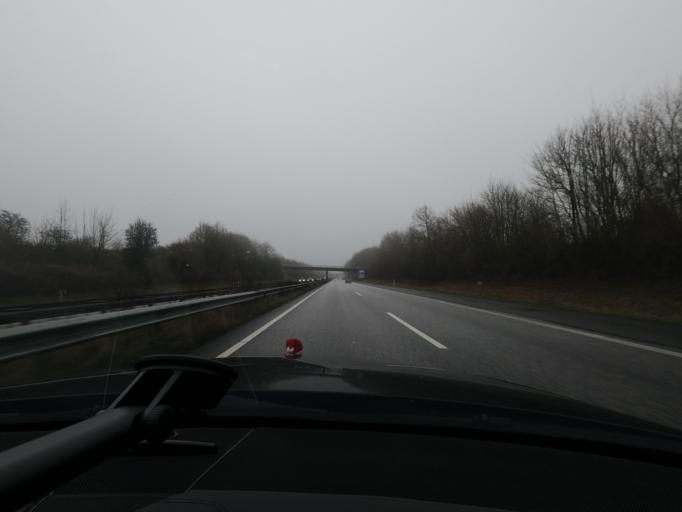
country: DE
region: Schleswig-Holstein
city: Dannewerk
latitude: 54.4988
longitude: 9.5131
